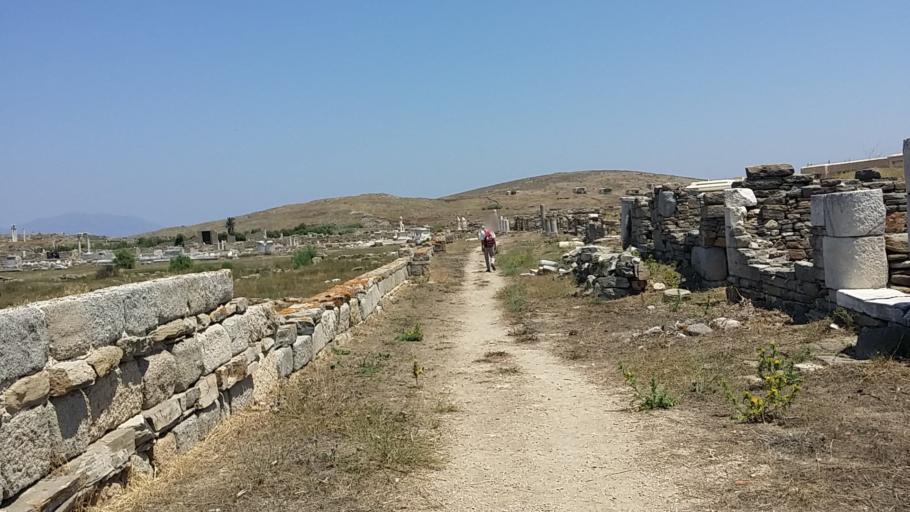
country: GR
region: South Aegean
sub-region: Nomos Kykladon
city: Mykonos
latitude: 37.4000
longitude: 25.2678
